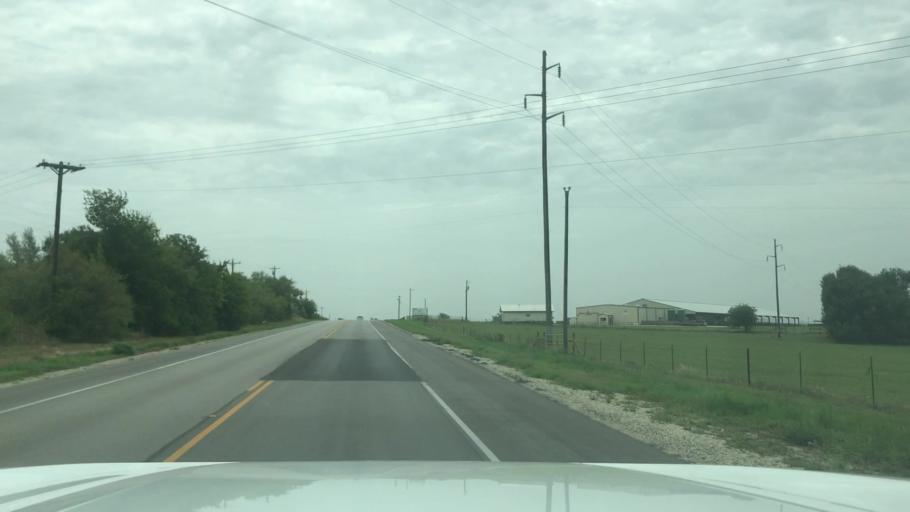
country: US
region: Texas
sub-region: Erath County
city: Dublin
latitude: 32.0874
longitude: -98.2574
